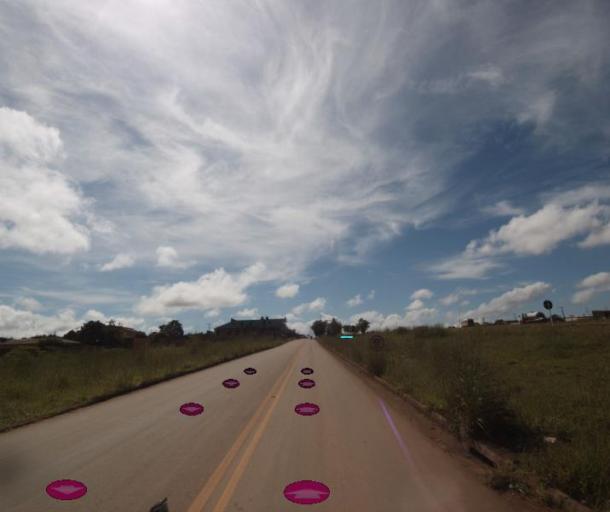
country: BR
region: Federal District
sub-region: Brasilia
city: Brasilia
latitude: -15.7380
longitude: -48.2975
